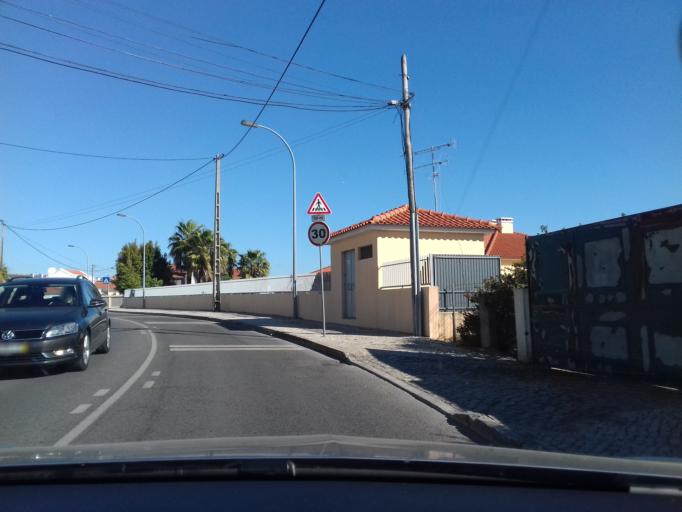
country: PT
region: Lisbon
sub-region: Cascais
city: Alcabideche
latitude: 38.7203
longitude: -9.4112
